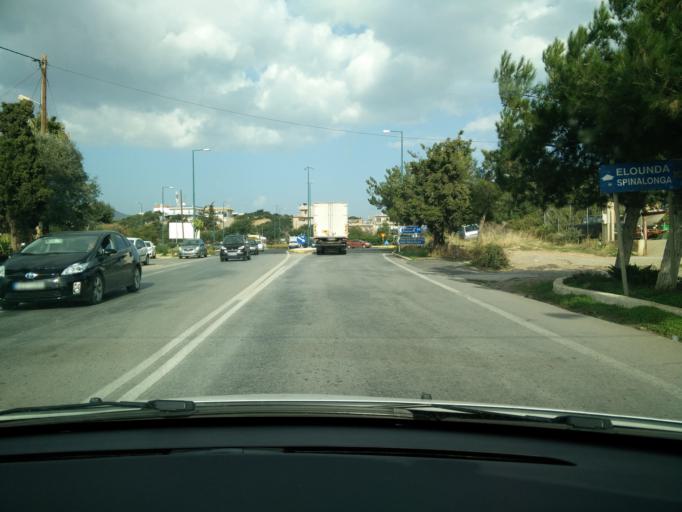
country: GR
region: Crete
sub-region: Nomos Lasithiou
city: Agios Nikolaos
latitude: 35.1989
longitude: 25.7060
